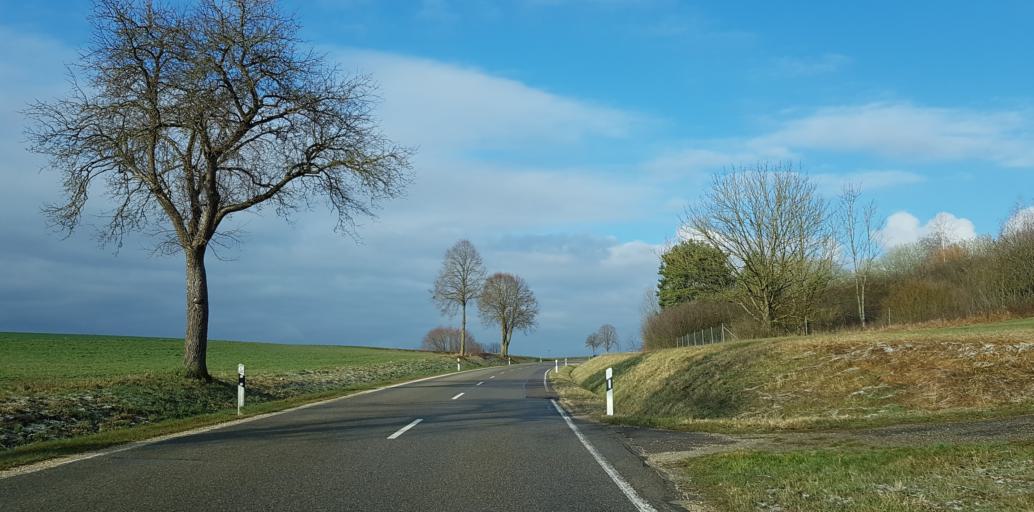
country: DE
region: Baden-Wuerttemberg
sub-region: Tuebingen Region
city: Altheim
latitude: 48.3272
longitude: 9.7850
